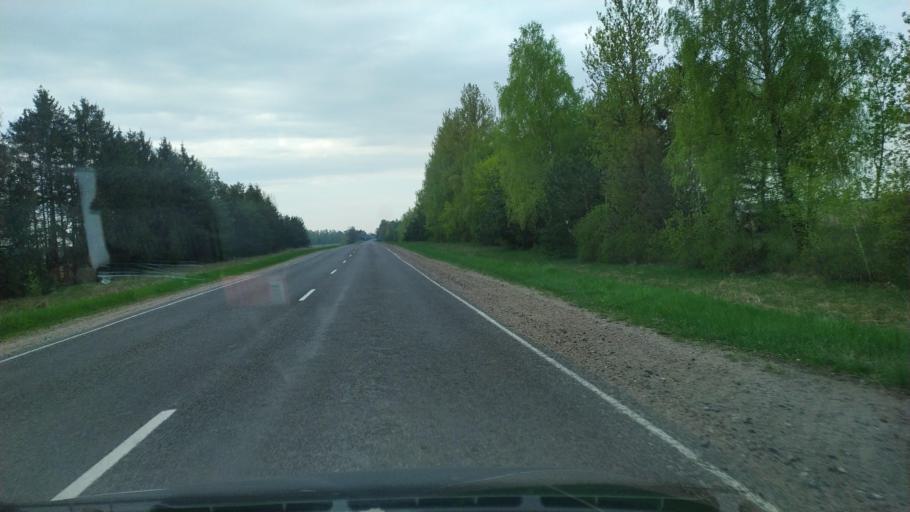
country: BY
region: Brest
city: Kamyanyets
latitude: 52.3521
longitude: 23.8986
